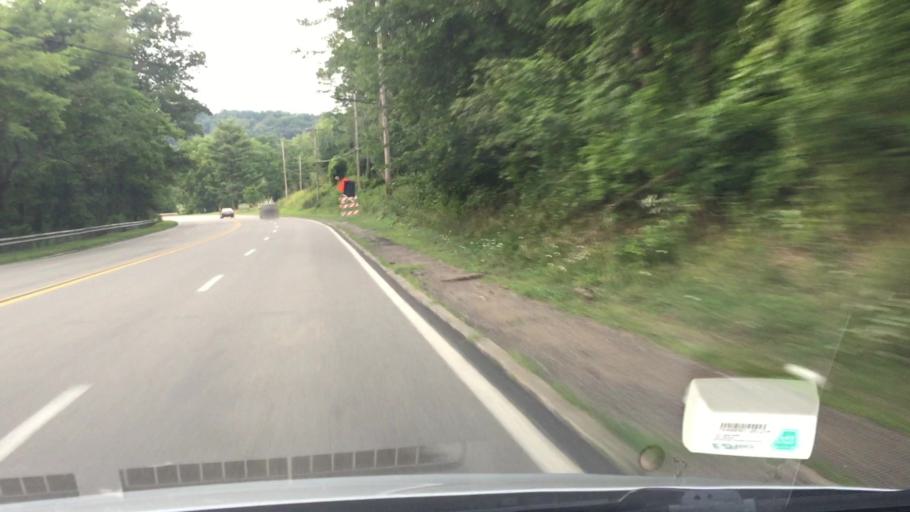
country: US
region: Pennsylvania
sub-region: Allegheny County
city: Allison Park
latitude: 40.5893
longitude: -79.9975
